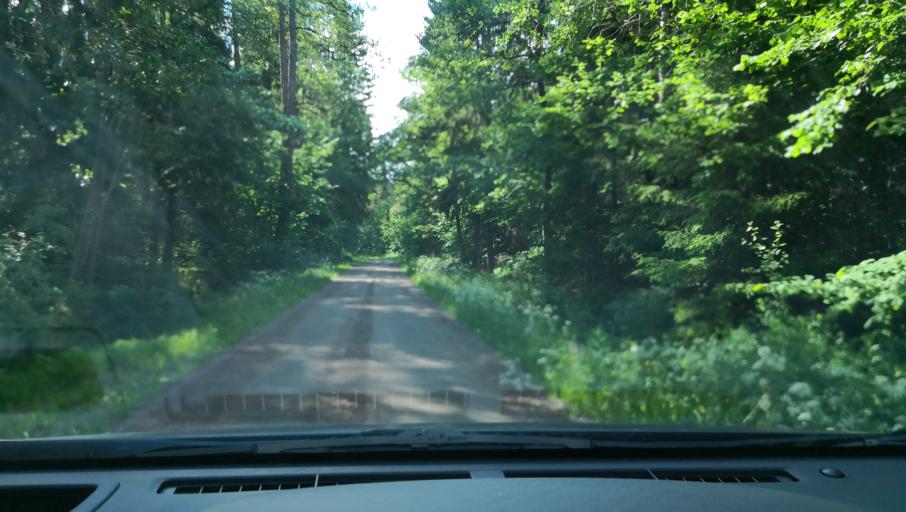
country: SE
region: Uppsala
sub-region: Enkopings Kommun
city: Orsundsbro
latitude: 59.8354
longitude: 17.2305
